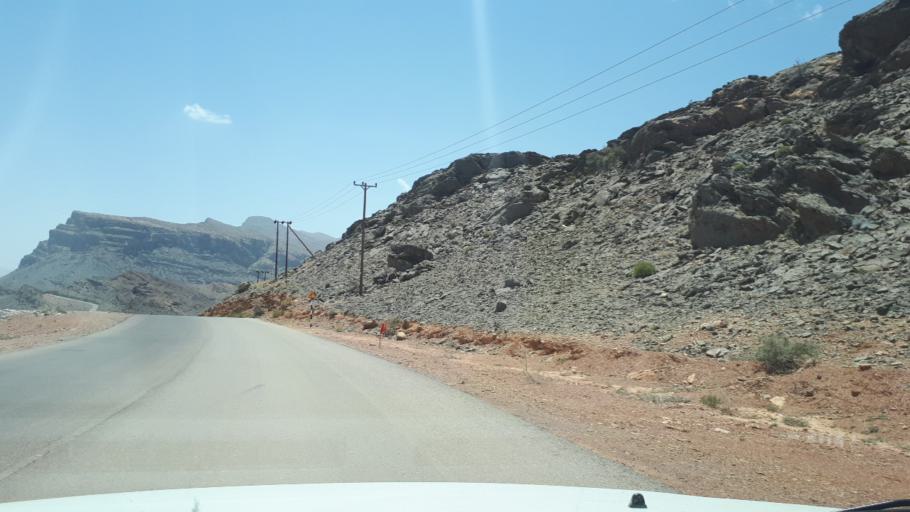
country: OM
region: Al Batinah
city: Rustaq
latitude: 23.2450
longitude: 57.1536
